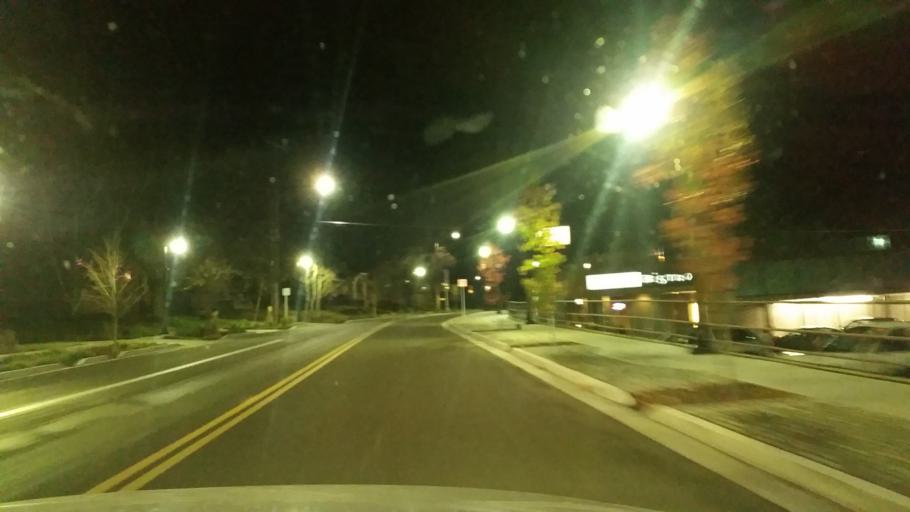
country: US
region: Washington
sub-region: Spokane County
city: Spokane
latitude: 47.6426
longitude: -117.4244
